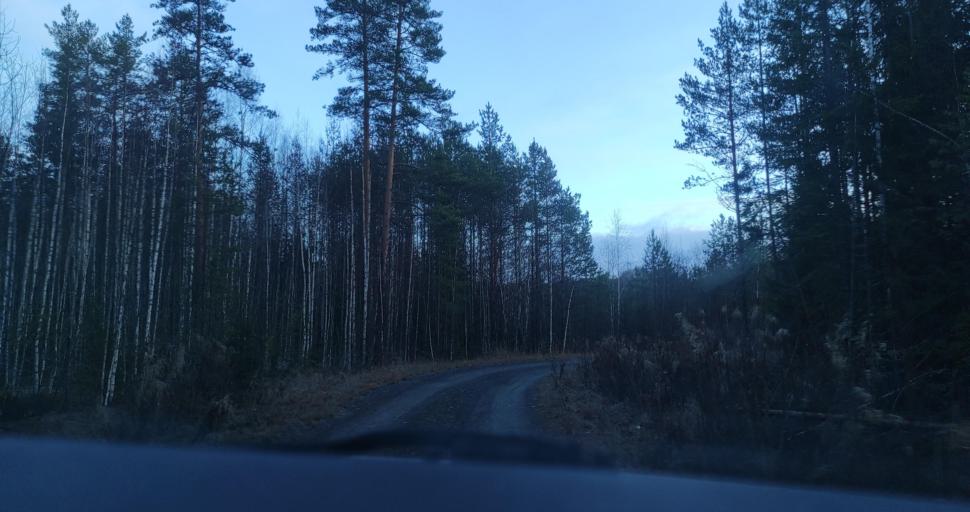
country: RU
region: Republic of Karelia
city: Pitkyaranta
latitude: 61.7345
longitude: 31.3713
